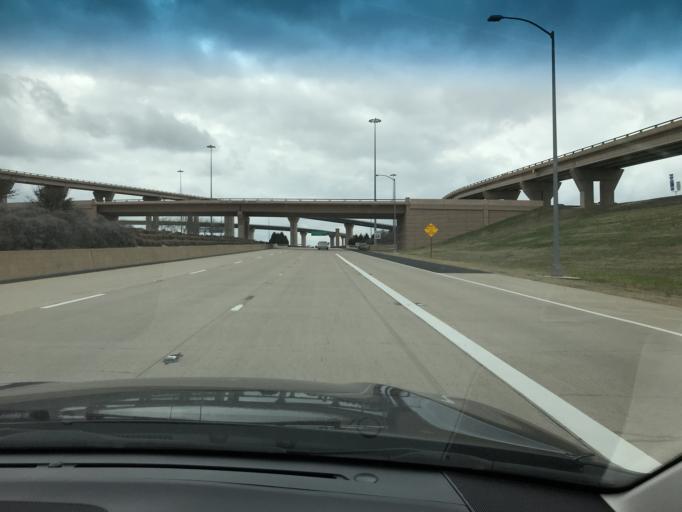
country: US
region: Texas
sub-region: Tarrant County
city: Benbrook
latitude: 32.6878
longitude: -97.4051
